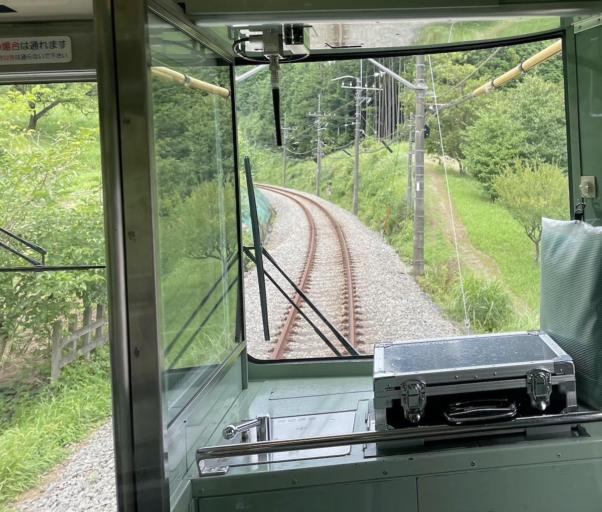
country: JP
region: Saitama
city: Morohongo
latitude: 35.9054
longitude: 139.2428
